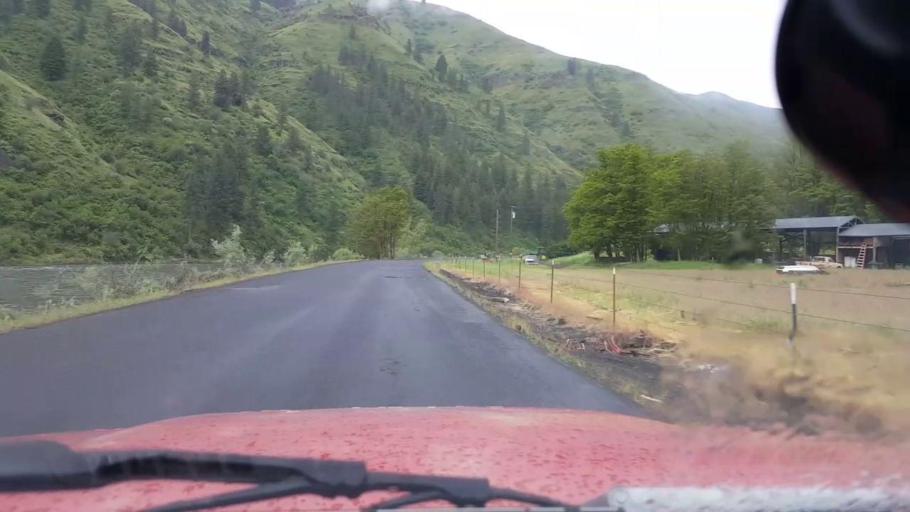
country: US
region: Washington
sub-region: Asotin County
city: Asotin
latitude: 46.0376
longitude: -117.2672
